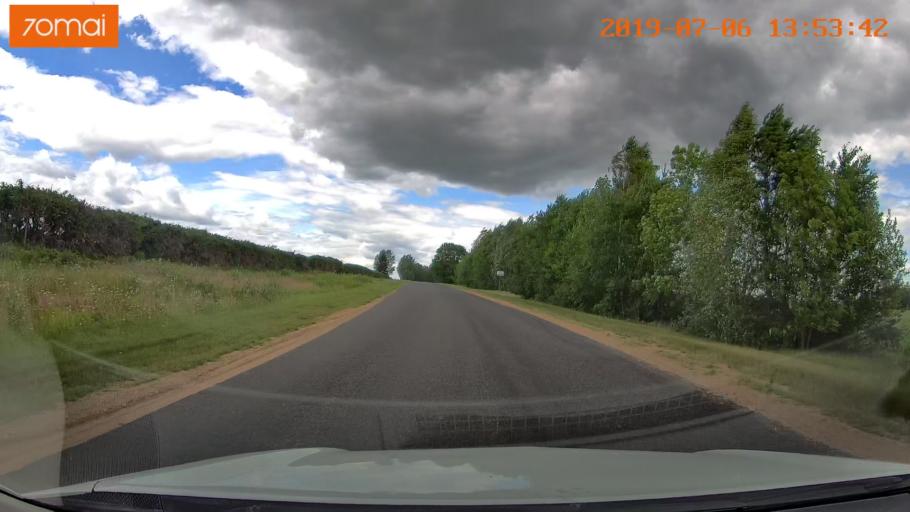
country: BY
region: Minsk
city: Ivyanyets
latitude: 53.7373
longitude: 26.8246
